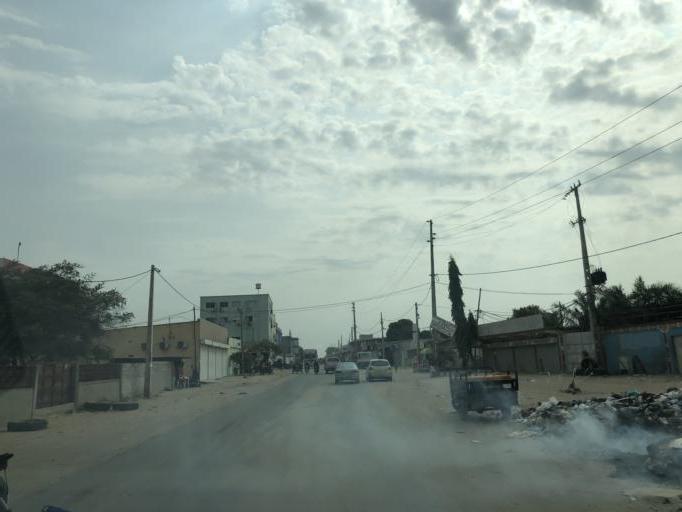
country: AO
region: Luanda
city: Luanda
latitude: -8.9061
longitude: 13.3435
